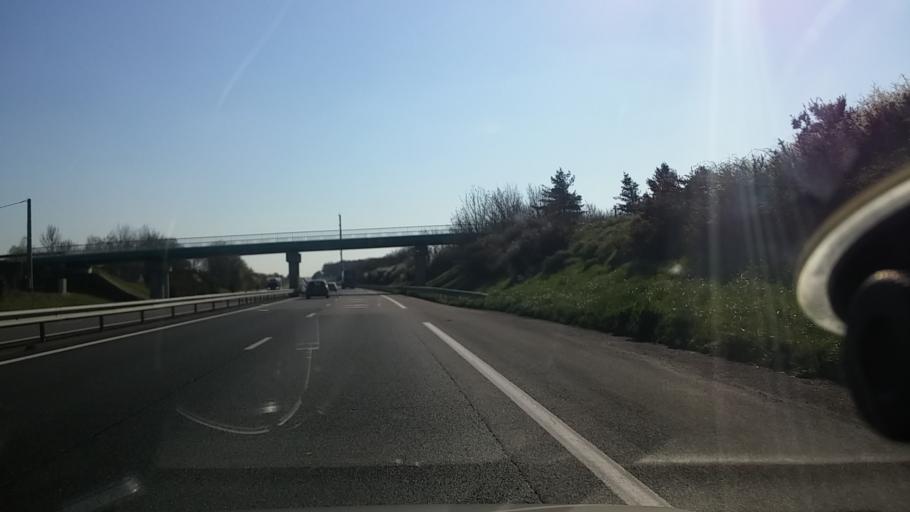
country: FR
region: Centre
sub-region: Departement du Cher
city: Massay
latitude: 47.1601
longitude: 1.9849
